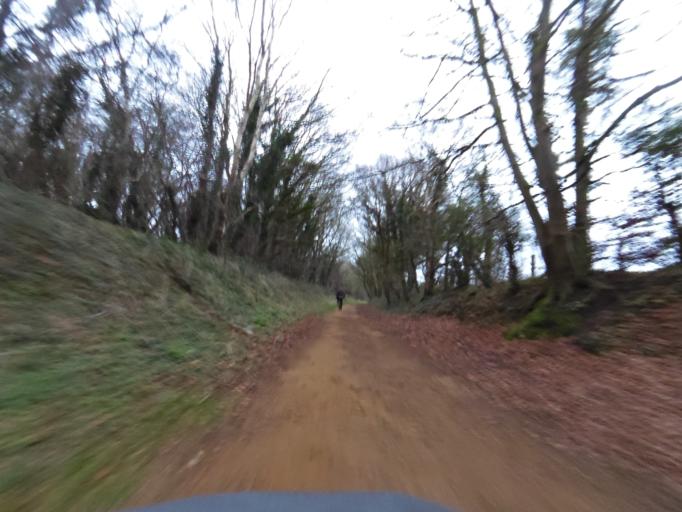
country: GB
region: England
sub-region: Norfolk
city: Horsford
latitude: 52.7041
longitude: 1.1919
